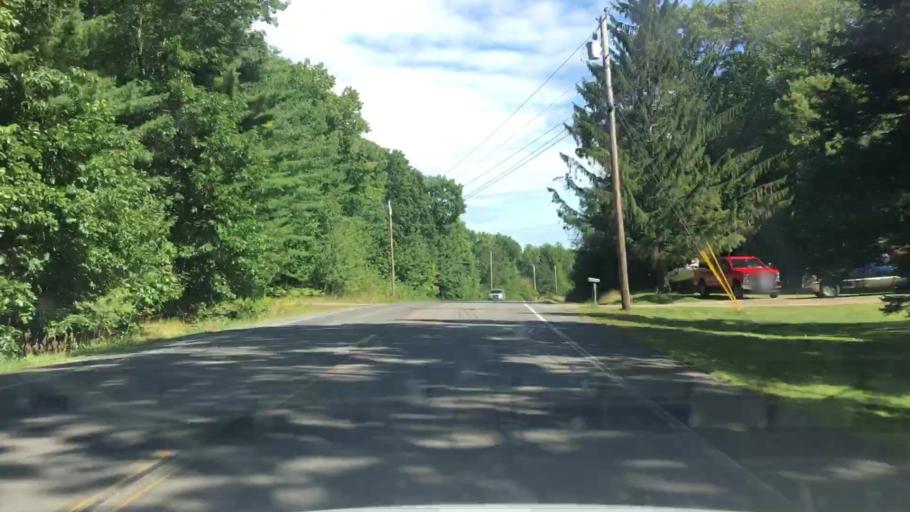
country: US
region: Maine
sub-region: Penobscot County
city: Garland
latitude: 45.0856
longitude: -69.2262
